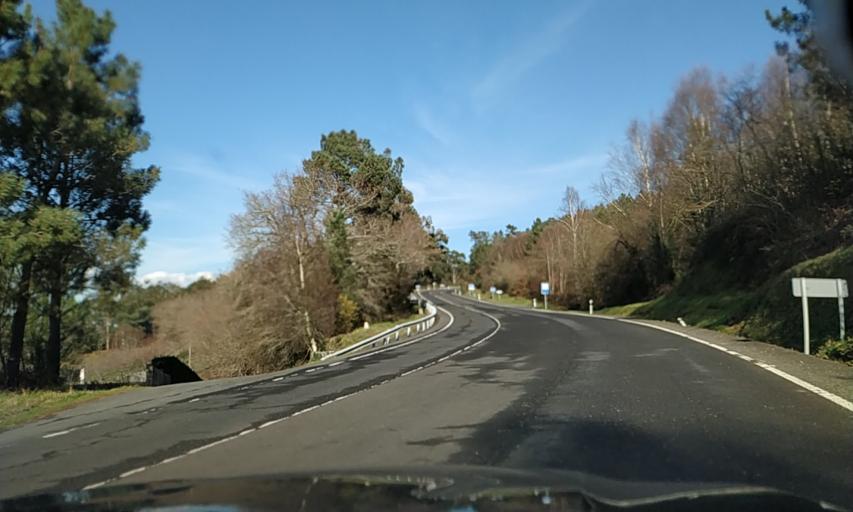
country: ES
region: Galicia
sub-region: Provincia da Coruna
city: Ribeira
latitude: 42.7132
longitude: -8.3693
